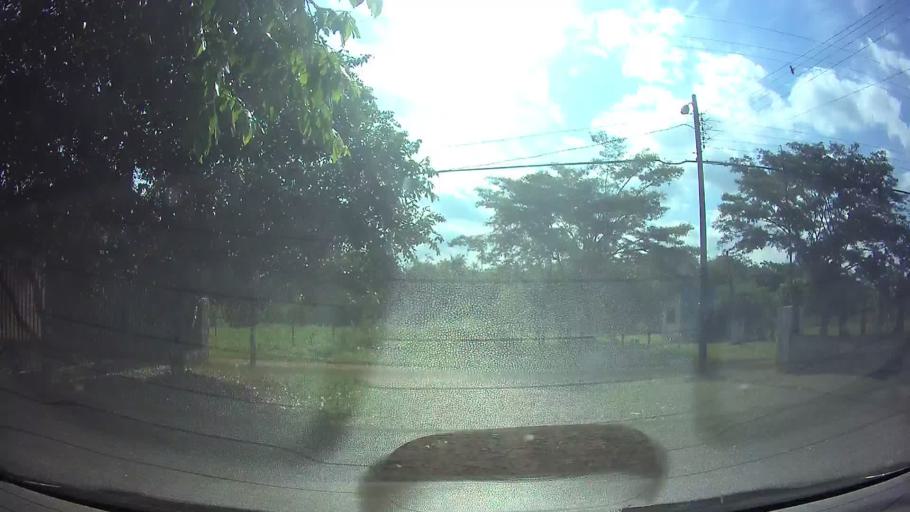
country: PY
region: Central
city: Limpio
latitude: -25.2477
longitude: -57.4694
